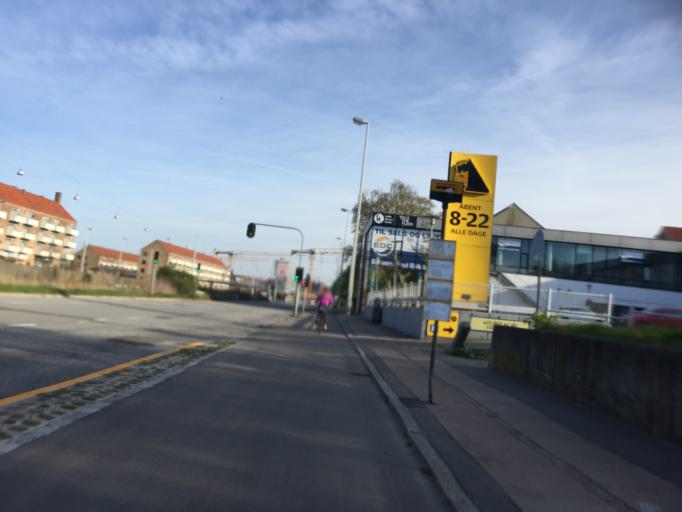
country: DK
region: Capital Region
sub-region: Kobenhavn
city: Copenhagen
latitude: 55.7200
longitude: 12.5557
